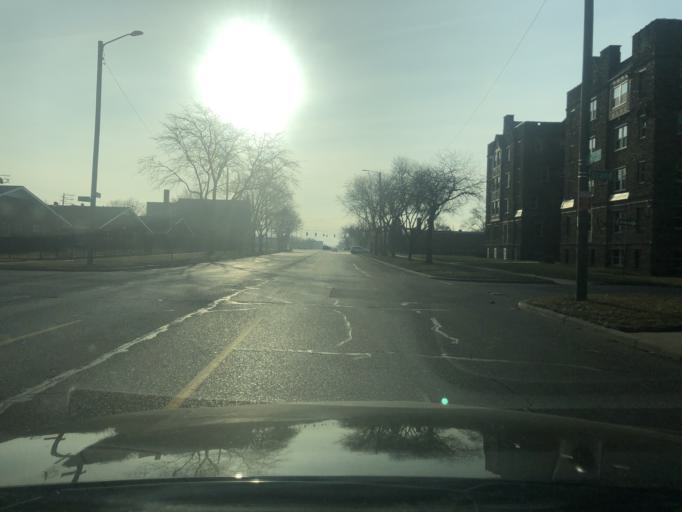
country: US
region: Michigan
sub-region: Wayne County
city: Highland Park
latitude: 42.3916
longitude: -83.1322
